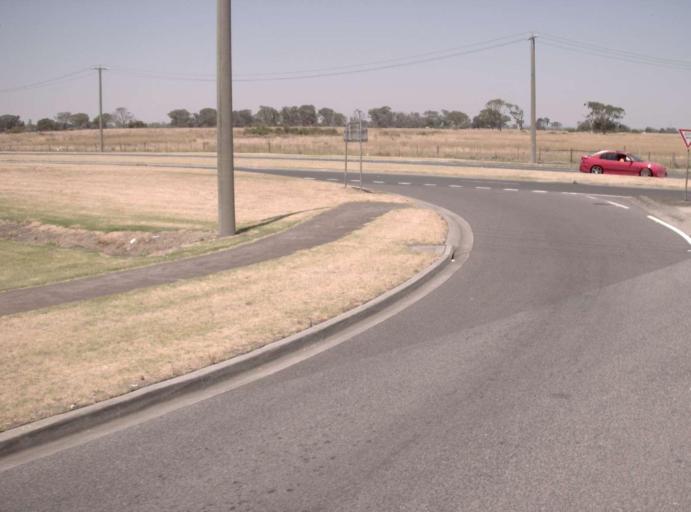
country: AU
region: Victoria
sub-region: Kingston
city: Waterways
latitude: -38.0104
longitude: 145.1410
